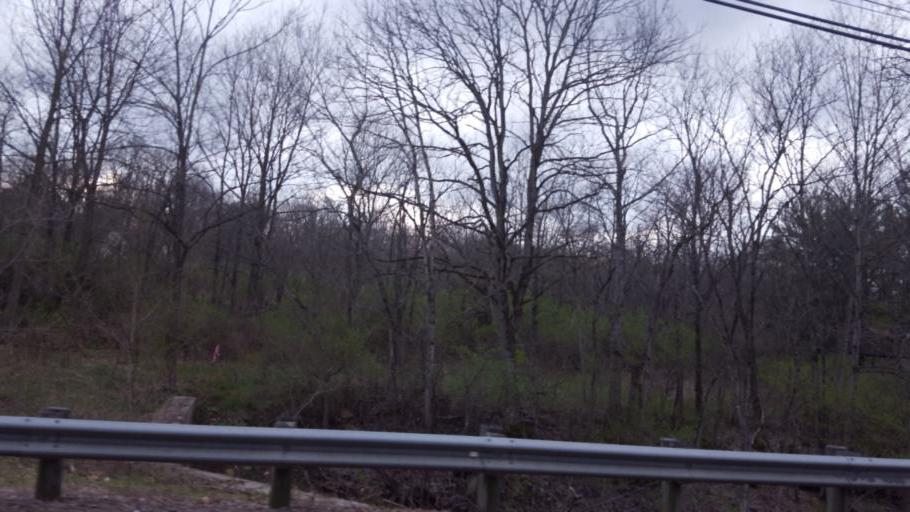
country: US
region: Ohio
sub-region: Delaware County
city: Delaware
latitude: 40.2547
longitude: -83.0635
